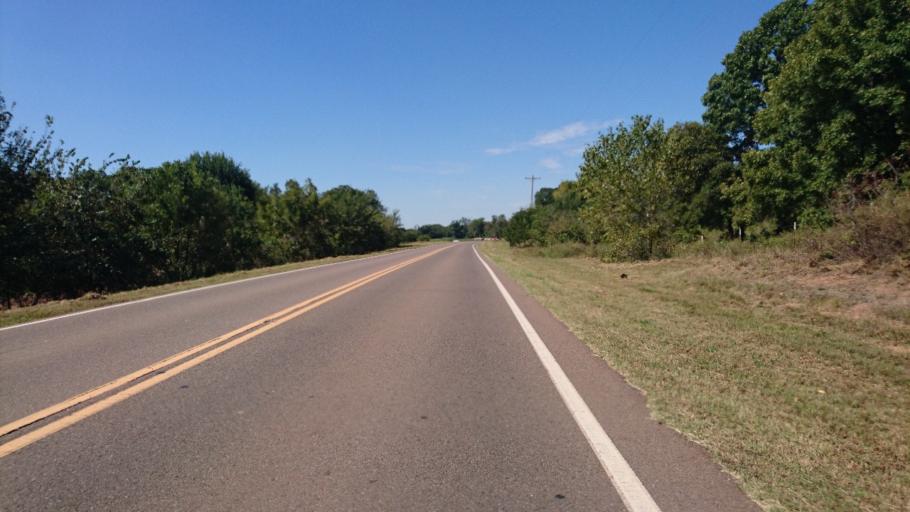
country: US
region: Oklahoma
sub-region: Oklahoma County
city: Luther
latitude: 35.6600
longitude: -97.2752
